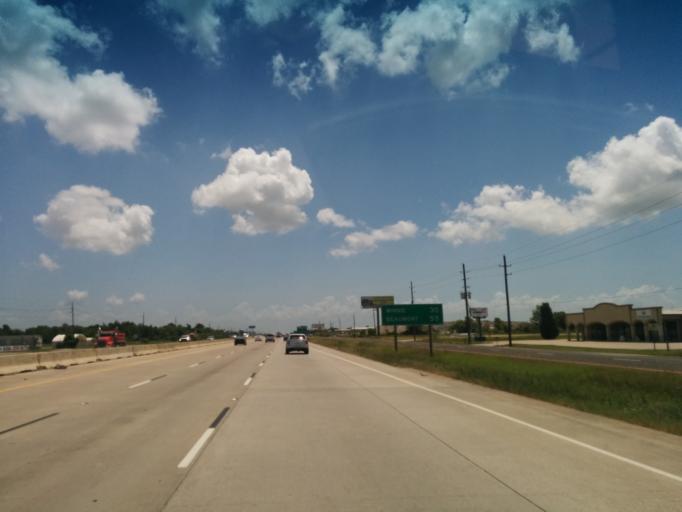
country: US
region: Texas
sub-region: Chambers County
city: Mont Belvieu
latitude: 29.8222
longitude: -94.8907
